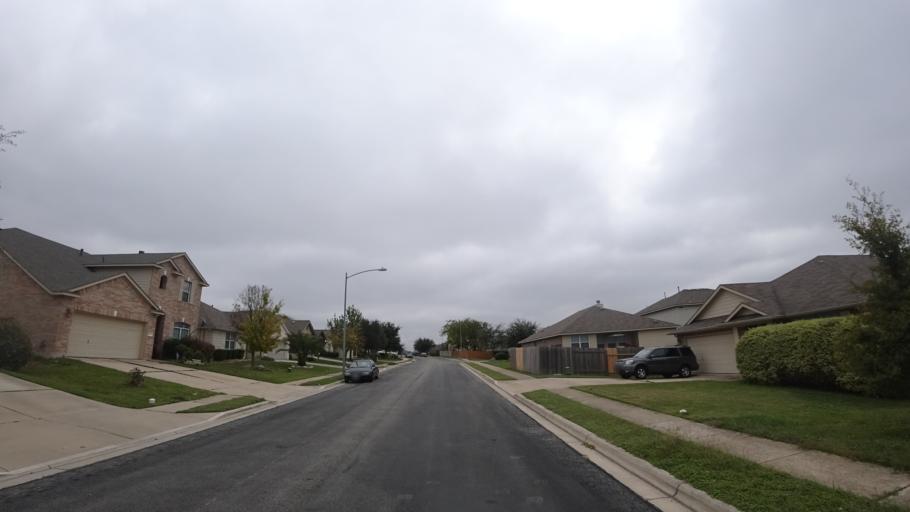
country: US
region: Texas
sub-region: Travis County
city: Pflugerville
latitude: 30.3762
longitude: -97.6501
